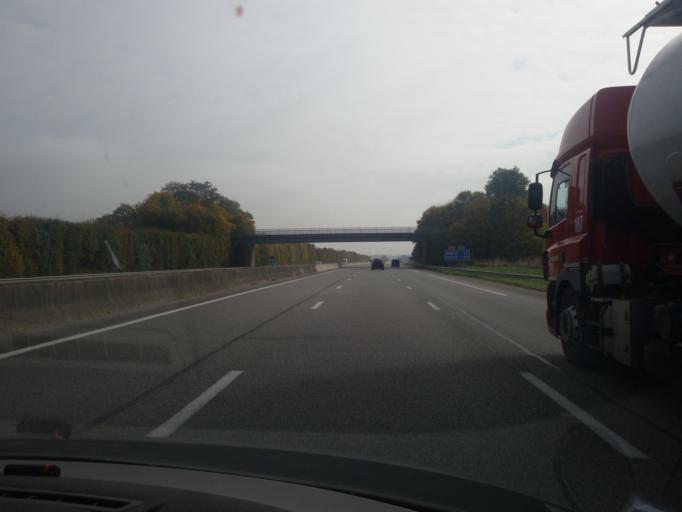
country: FR
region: Haute-Normandie
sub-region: Departement de l'Eure
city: Saint-Aubin-sur-Gaillon
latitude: 49.1245
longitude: 1.3257
